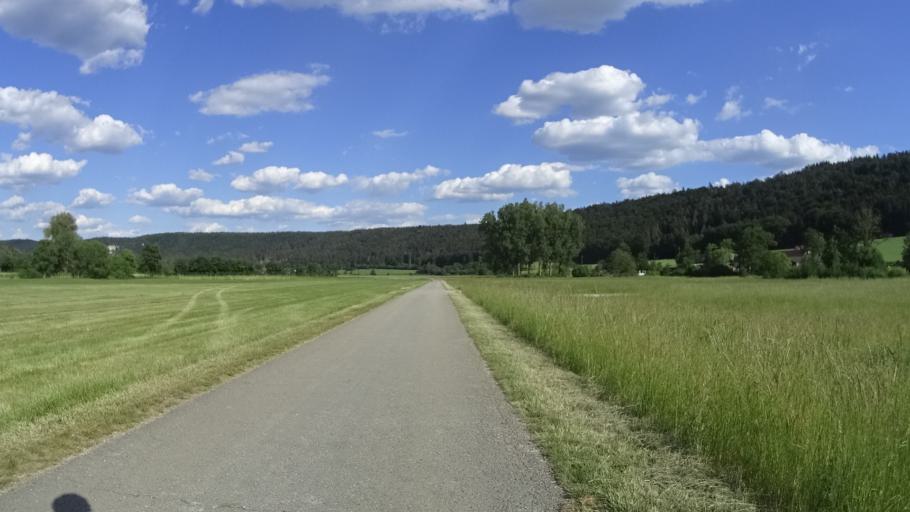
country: DE
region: Bavaria
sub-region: Upper Palatinate
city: Dietfurt
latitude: 49.0149
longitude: 11.5291
